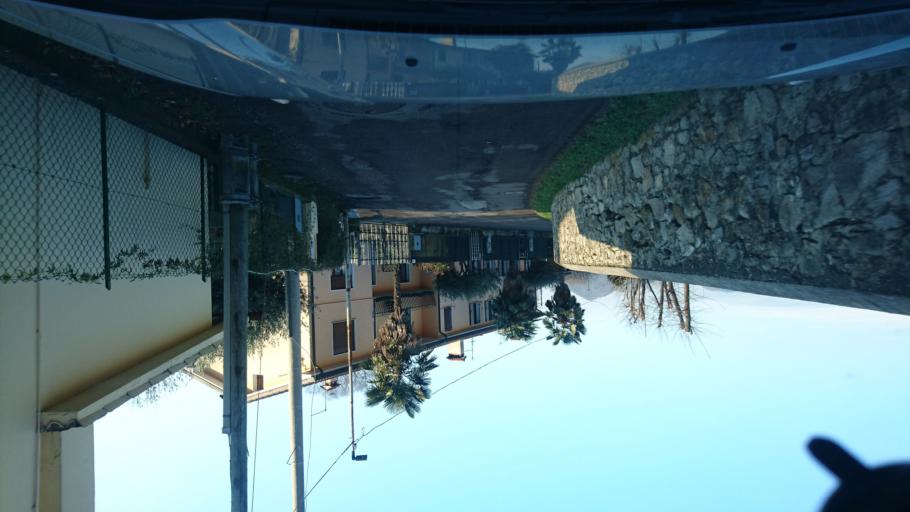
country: IT
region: Veneto
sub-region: Provincia di Padova
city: Torreglia
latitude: 45.3275
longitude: 11.7275
